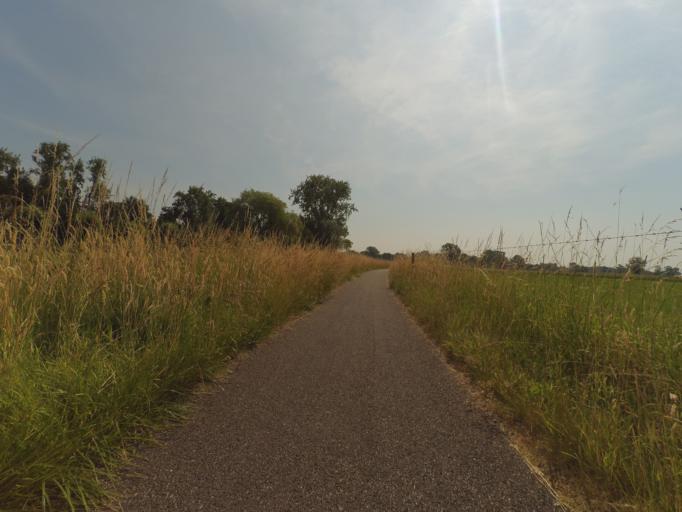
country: NL
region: North Brabant
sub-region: Gemeente Breda
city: Breda
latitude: 51.5277
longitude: 4.7826
